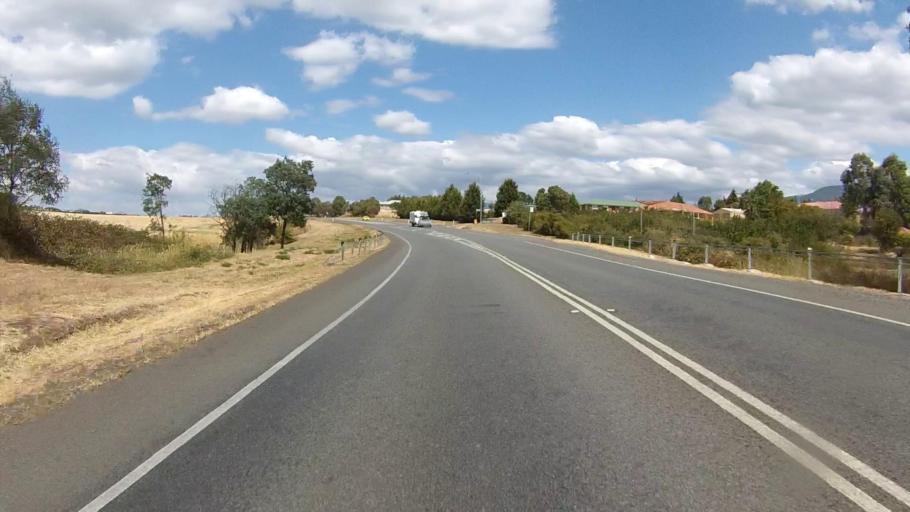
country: AU
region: Tasmania
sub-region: Glenorchy
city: Austins Ferry
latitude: -42.7570
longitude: 147.2680
